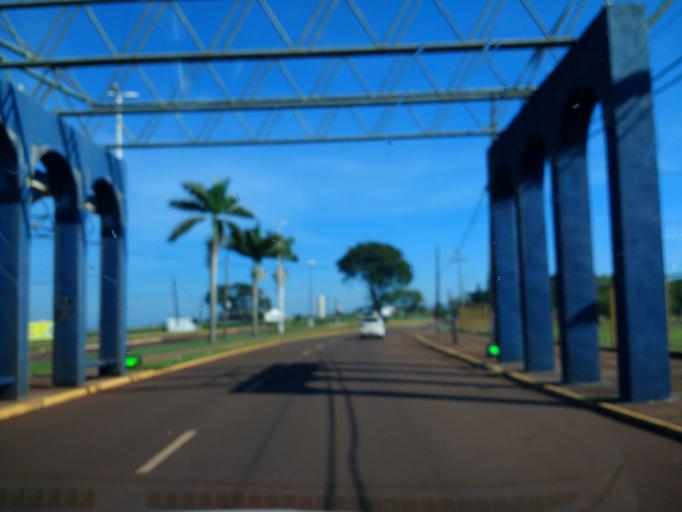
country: BR
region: Parana
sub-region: Palotina
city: Palotina
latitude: -24.4089
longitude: -53.5329
